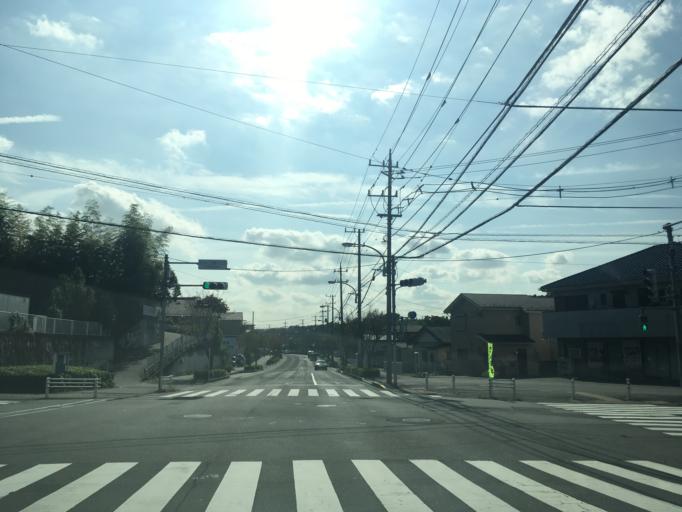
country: JP
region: Tokyo
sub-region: Machida-shi
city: Machida
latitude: 35.5901
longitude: 139.4184
